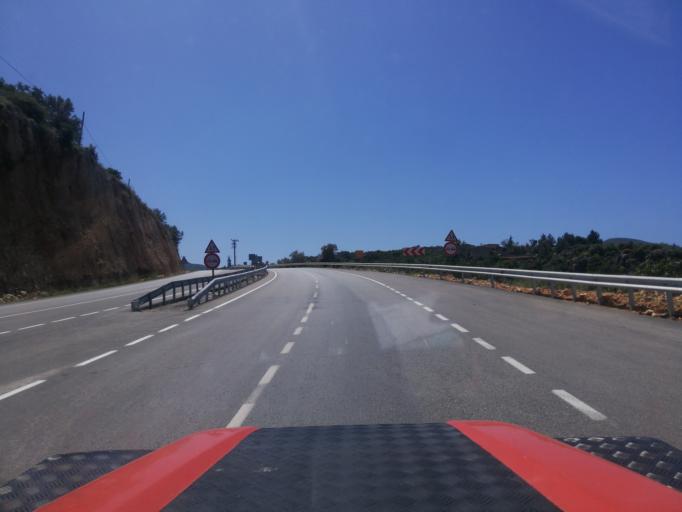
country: TR
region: Antalya
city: Kalkan
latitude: 36.2553
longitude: 29.4198
